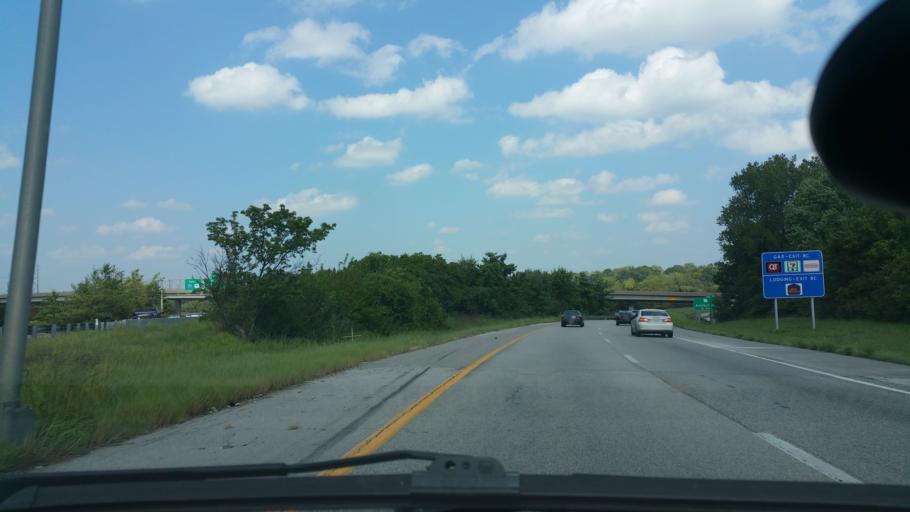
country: US
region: Missouri
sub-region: Clay County
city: Gladstone
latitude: 39.1684
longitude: -94.5578
